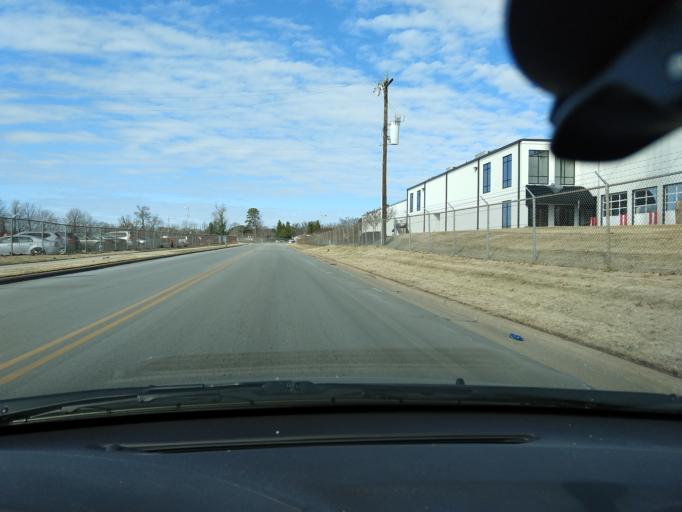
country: US
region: North Carolina
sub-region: Guilford County
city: Greensboro
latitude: 36.0657
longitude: -79.8705
